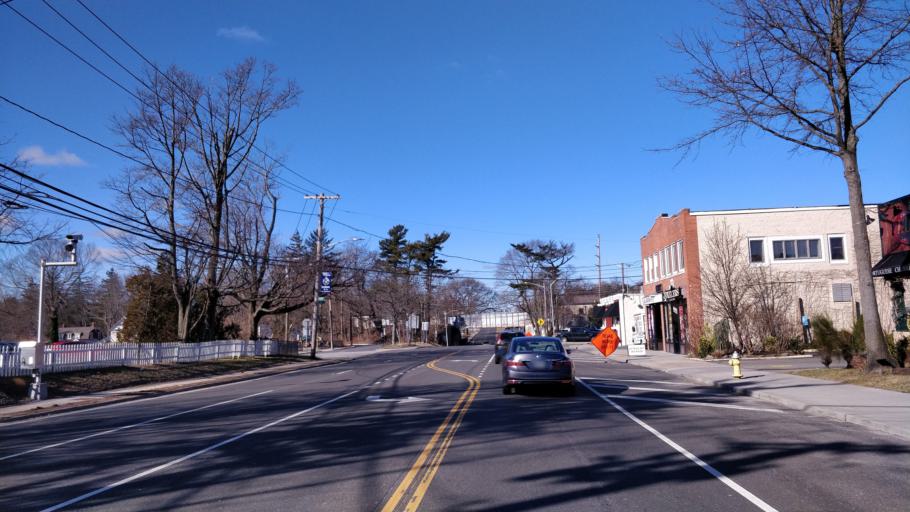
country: US
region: New York
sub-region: Suffolk County
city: Smithtown
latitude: 40.8554
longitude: -73.1990
